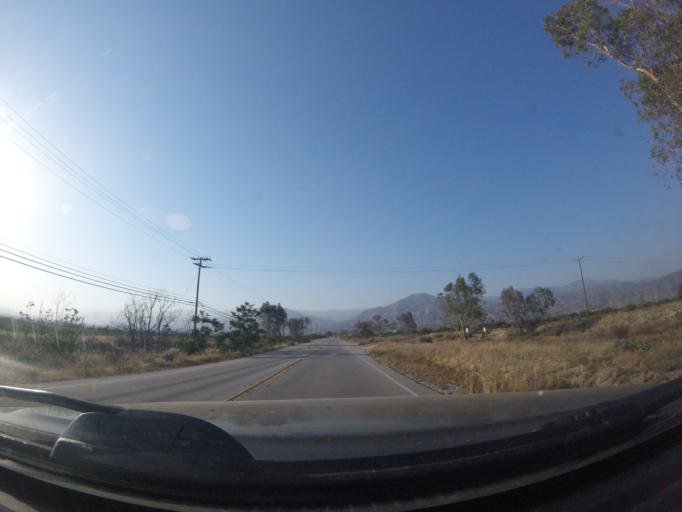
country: US
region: California
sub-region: San Bernardino County
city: Redlands
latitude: 34.0912
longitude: -117.1824
